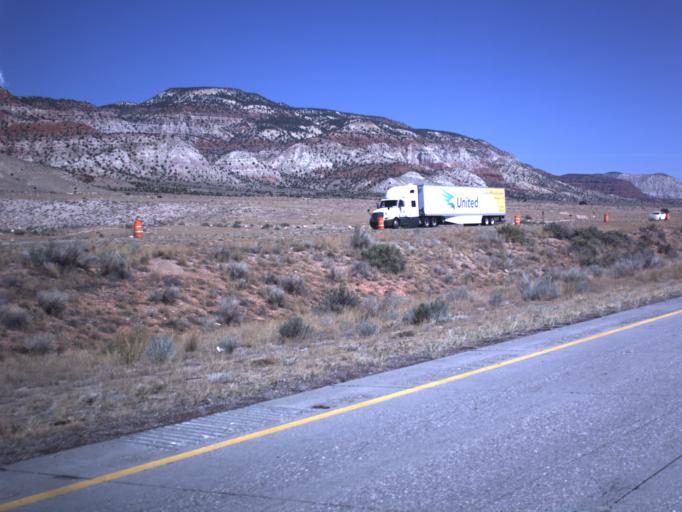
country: US
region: Utah
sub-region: Sevier County
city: Richfield
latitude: 38.8143
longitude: -112.0529
